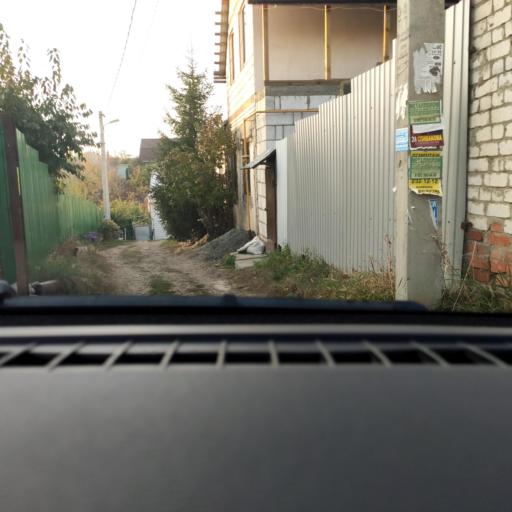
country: RU
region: Voronezj
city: Voronezh
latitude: 51.6268
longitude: 39.1952
